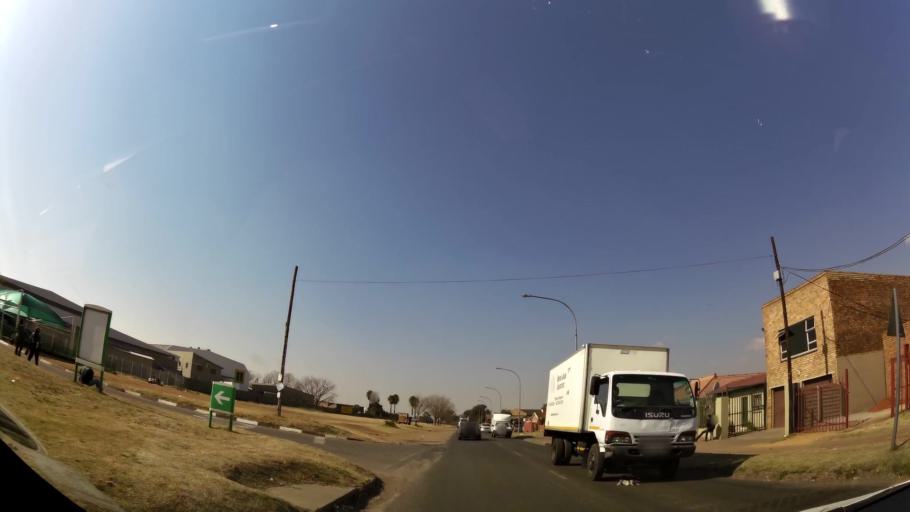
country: ZA
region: Gauteng
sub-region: Ekurhuleni Metropolitan Municipality
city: Benoni
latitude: -26.2082
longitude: 28.3075
